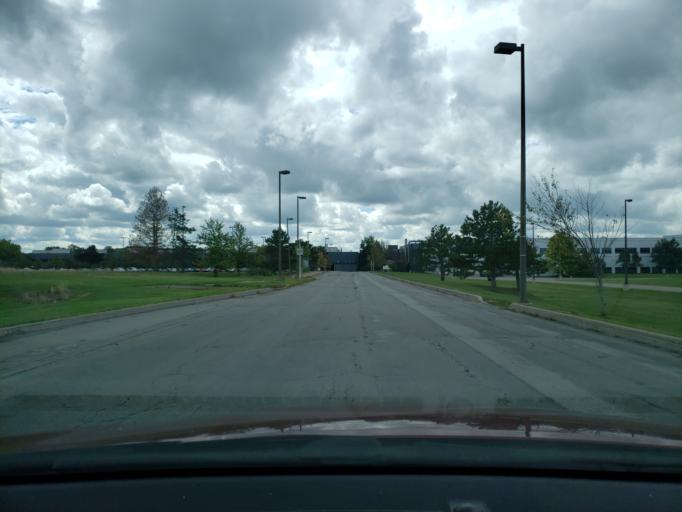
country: US
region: New York
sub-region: Monroe County
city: North Gates
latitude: 43.1559
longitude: -77.7464
